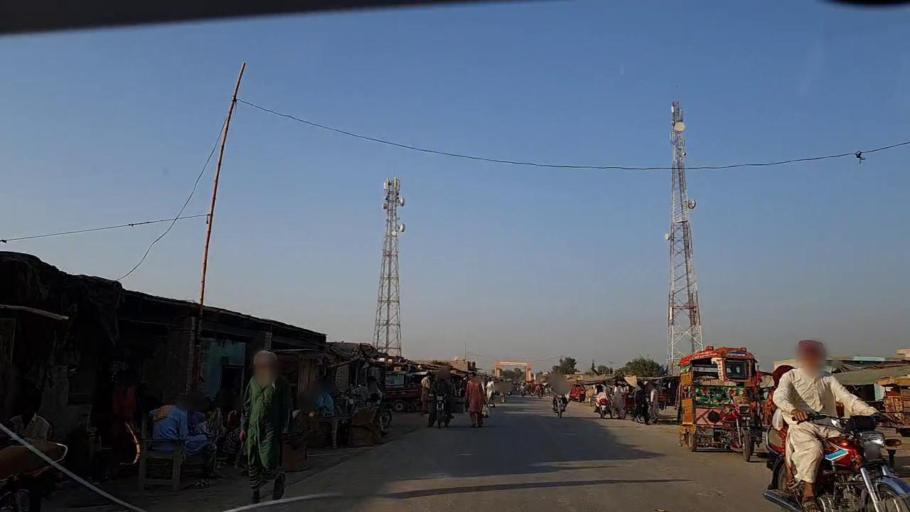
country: PK
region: Sindh
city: Rustam jo Goth
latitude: 28.0194
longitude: 68.8121
